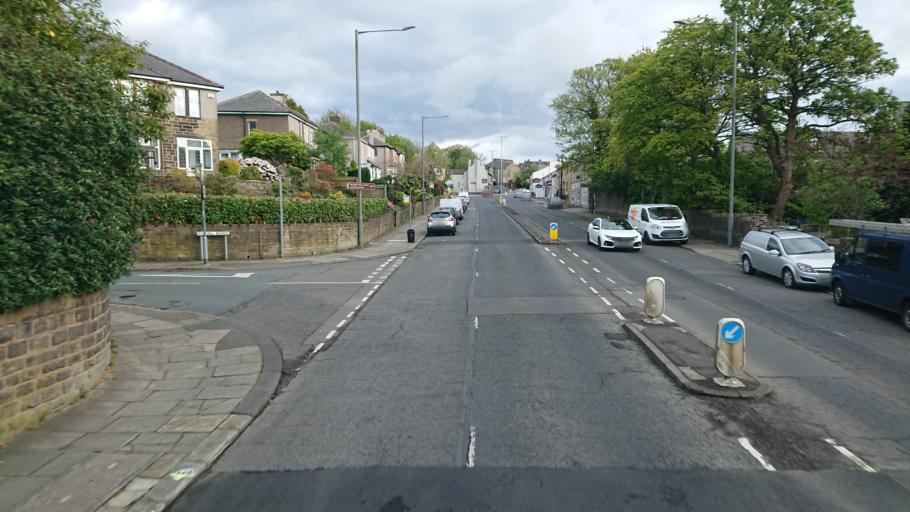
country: GB
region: England
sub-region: Lancashire
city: Burnley
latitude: 53.7794
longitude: -2.2543
